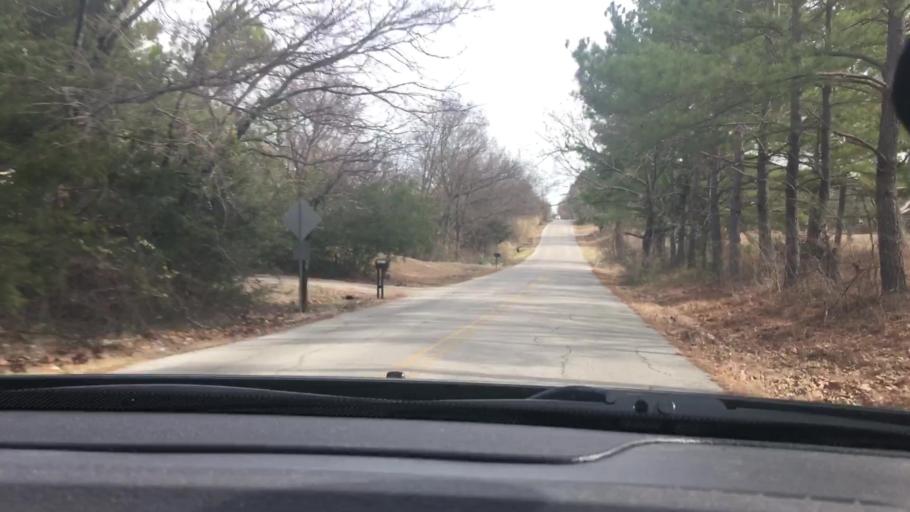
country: US
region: Oklahoma
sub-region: Carter County
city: Ardmore
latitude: 34.1728
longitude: -97.0772
